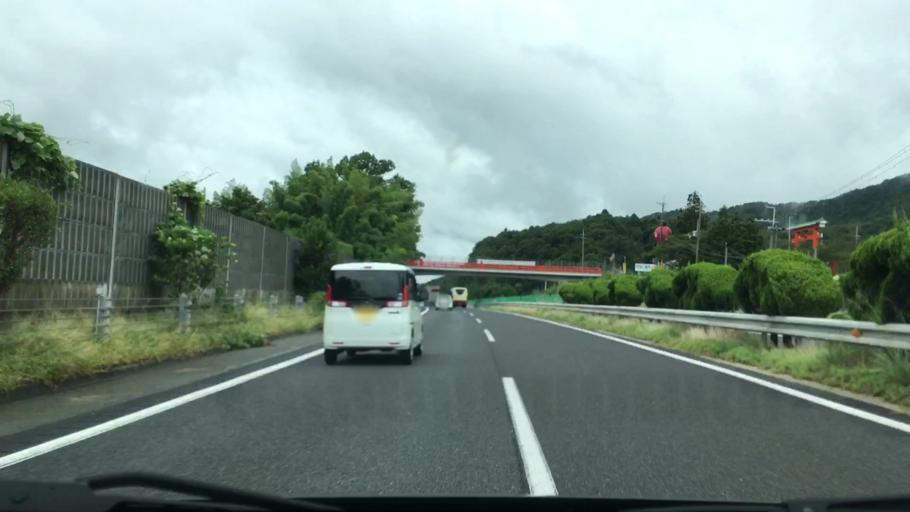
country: JP
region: Hyogo
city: Yamazakicho-nakabirose
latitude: 34.9896
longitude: 134.5927
